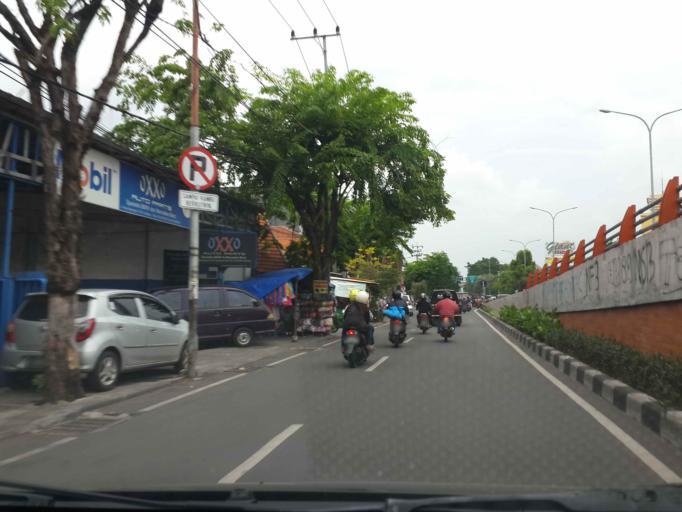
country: ID
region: East Java
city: Gubengairlangga
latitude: -7.2768
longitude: 112.7282
